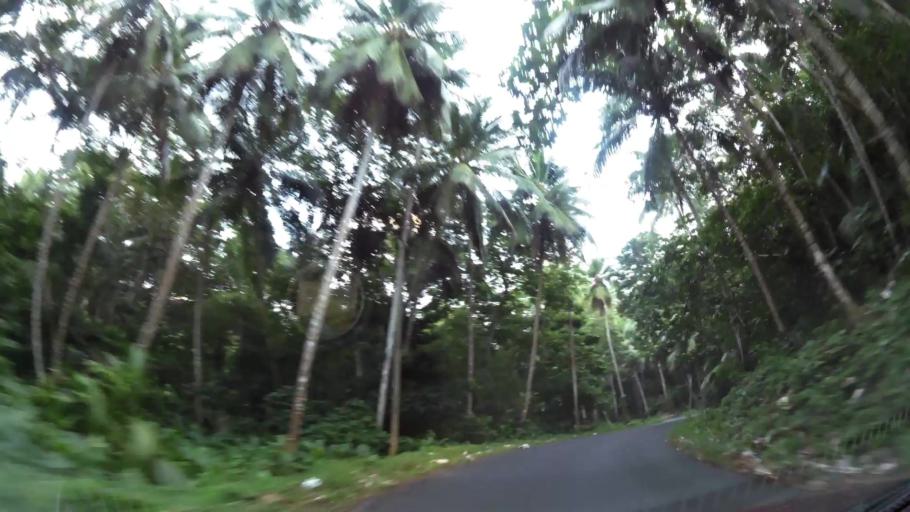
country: DM
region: Saint Andrew
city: Calibishie
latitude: 15.5912
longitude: -61.3617
